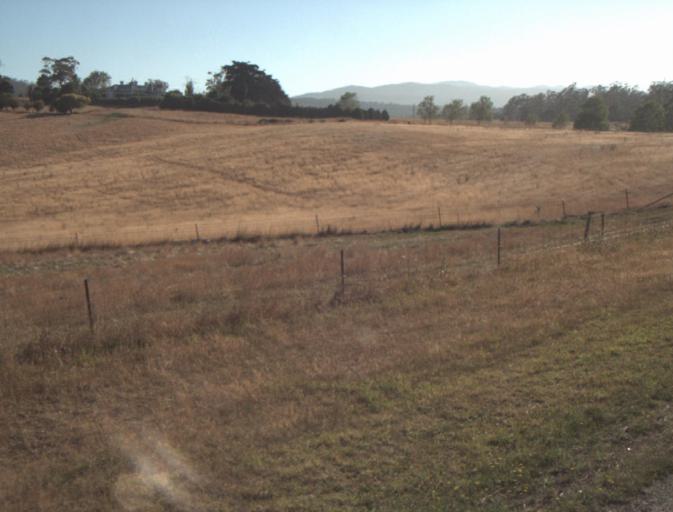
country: AU
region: Tasmania
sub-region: Launceston
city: Newstead
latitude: -41.4465
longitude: 147.2244
